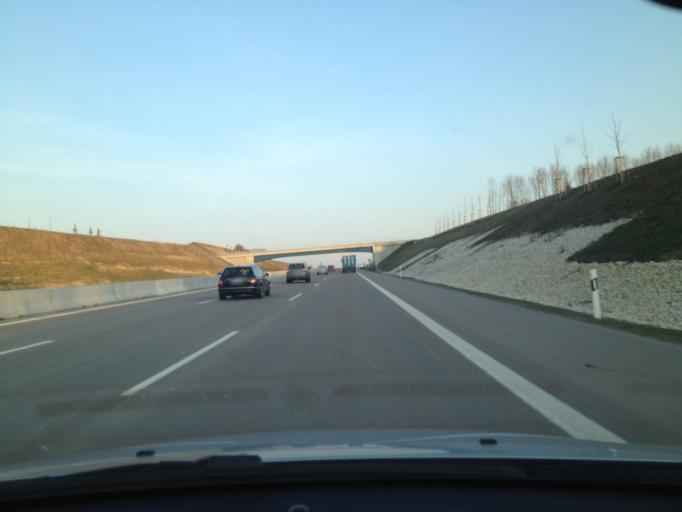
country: DE
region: Bavaria
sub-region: Swabia
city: Burgau
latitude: 48.4265
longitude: 10.3818
